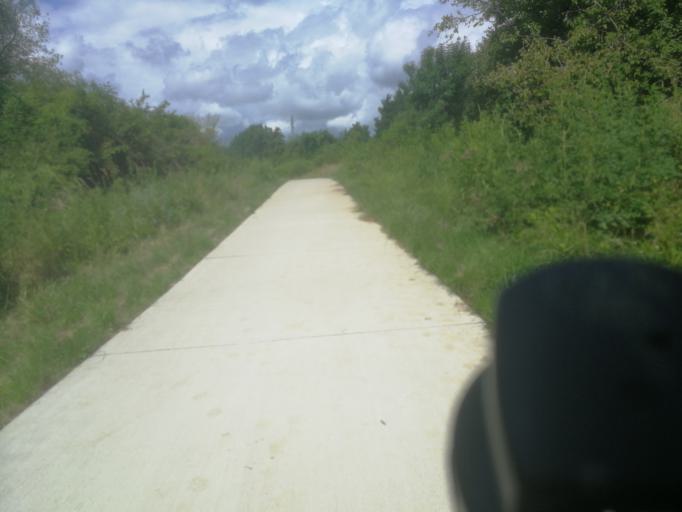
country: FR
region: Lorraine
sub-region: Departement de la Moselle
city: Gandrange
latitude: 49.2651
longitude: 6.1186
